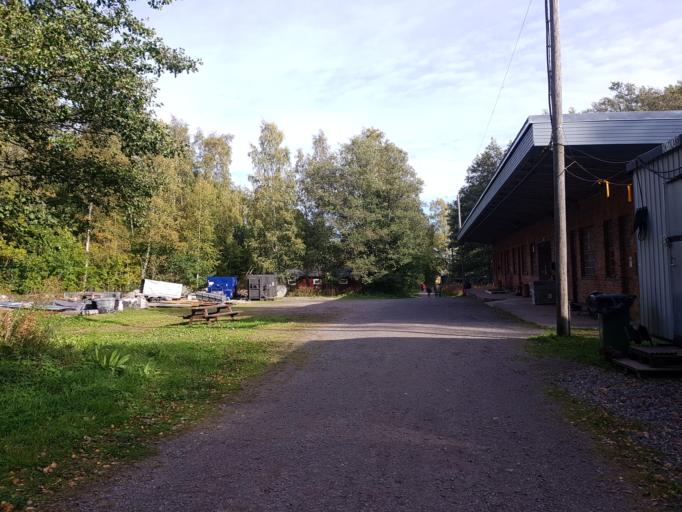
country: FI
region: Uusimaa
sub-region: Helsinki
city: Helsinki
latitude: 60.1375
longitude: 25.0066
